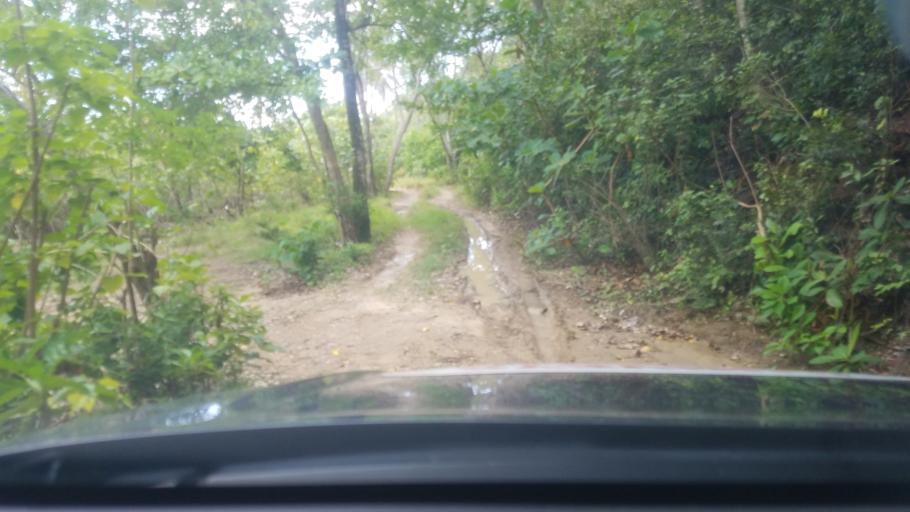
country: LC
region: Praslin
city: Praslin
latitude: 13.8692
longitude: -60.8925
